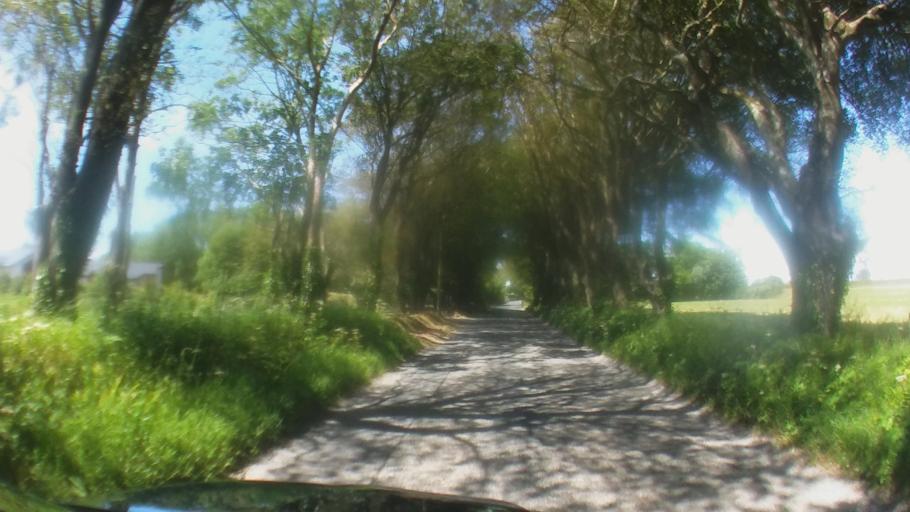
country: IE
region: Leinster
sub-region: Loch Garman
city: Loch Garman
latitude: 52.2330
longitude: -6.5630
